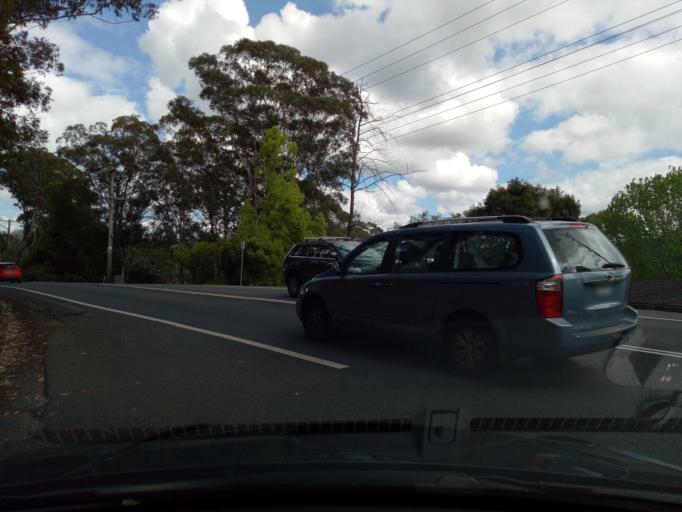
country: AU
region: New South Wales
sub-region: Gosford Shire
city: Narara
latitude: -33.3958
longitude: 151.3462
